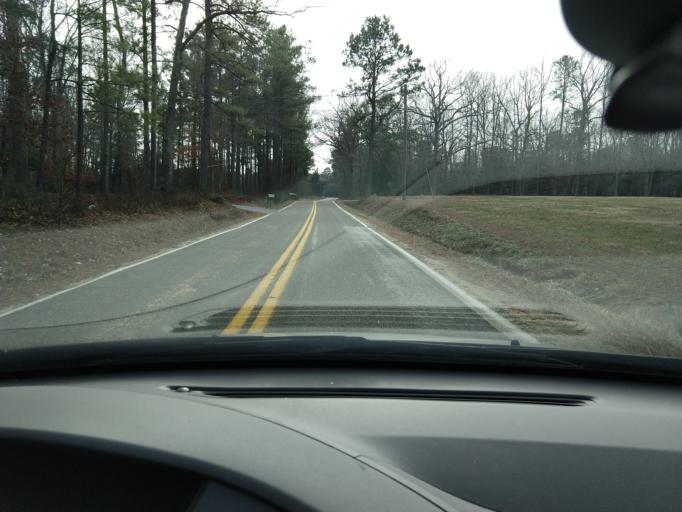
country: US
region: Virginia
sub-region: Henrico County
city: Fort Lee
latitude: 37.4333
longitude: -77.2359
